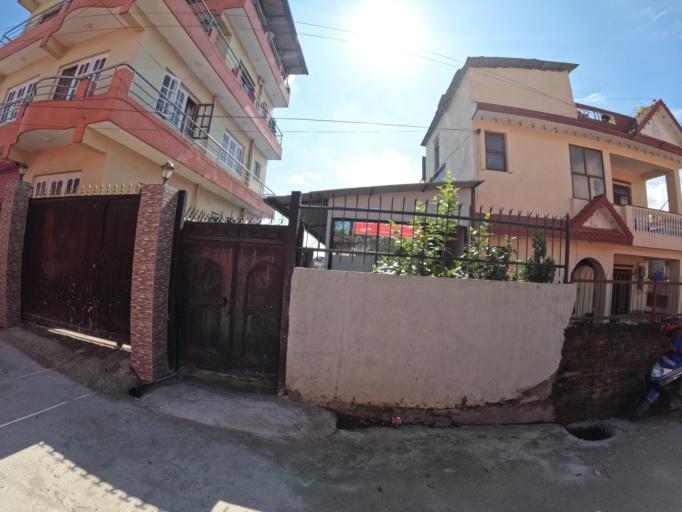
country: NP
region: Central Region
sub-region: Bagmati Zone
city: Kathmandu
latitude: 27.7481
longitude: 85.3357
